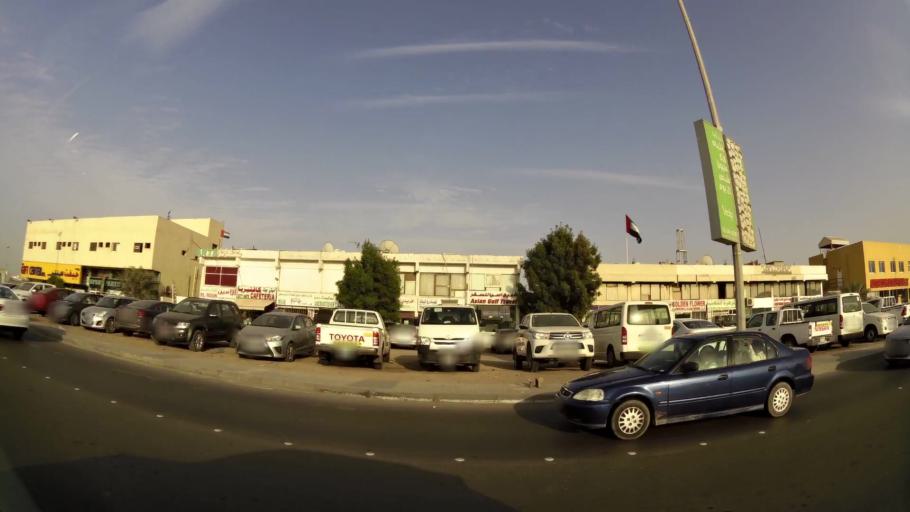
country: AE
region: Abu Dhabi
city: Abu Dhabi
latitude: 24.3724
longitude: 54.5113
